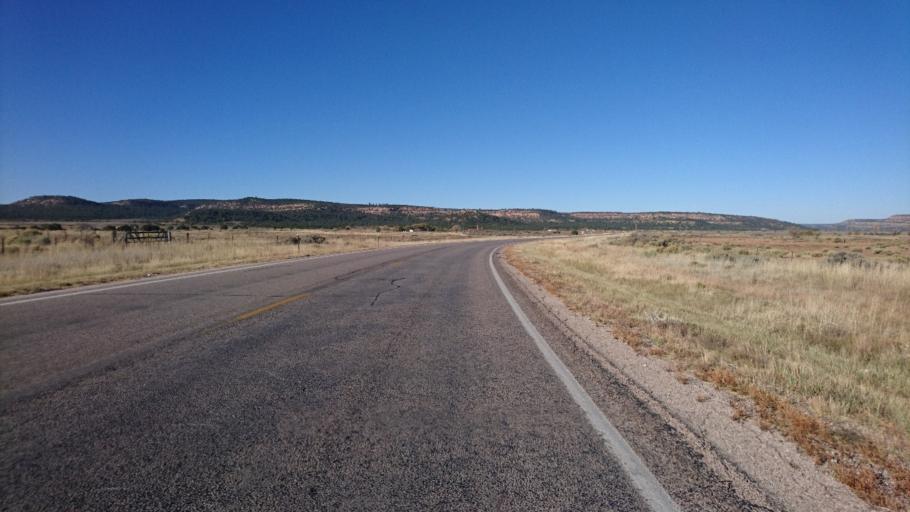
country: US
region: New Mexico
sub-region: McKinley County
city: Black Rock
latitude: 35.1058
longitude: -108.5696
